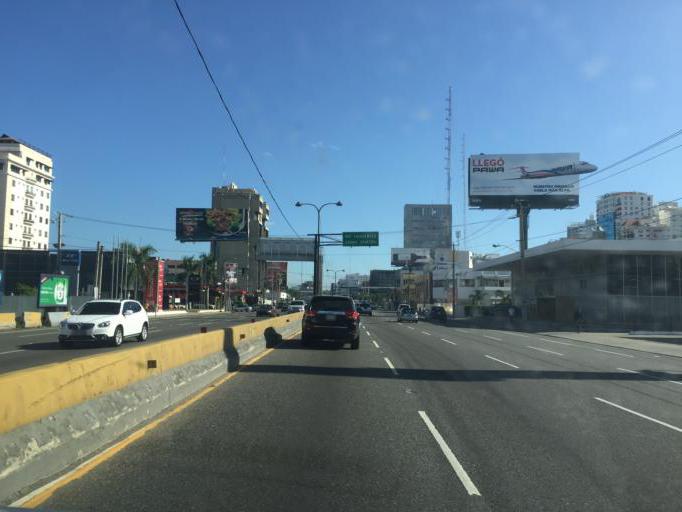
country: DO
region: Nacional
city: La Julia
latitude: 18.4673
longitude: -69.9268
